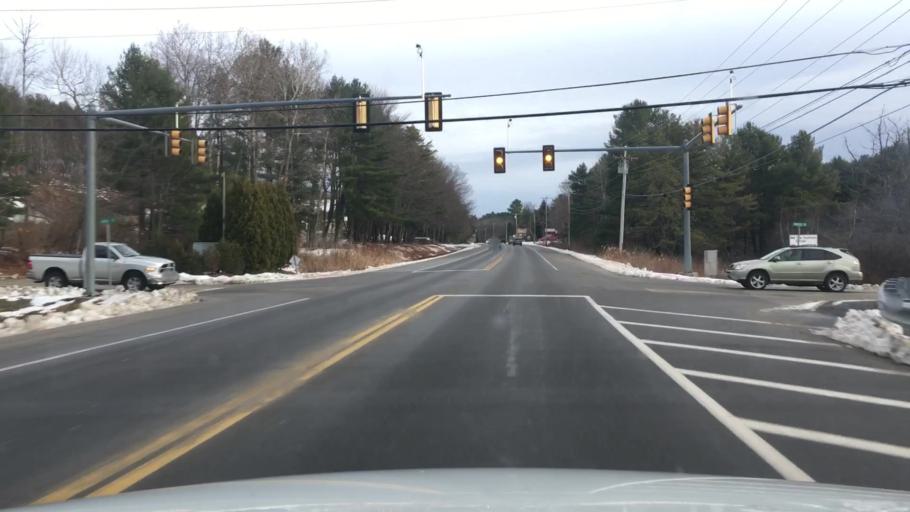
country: US
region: Maine
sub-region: Cumberland County
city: Falmouth Foreside
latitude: 43.7398
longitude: -70.2207
